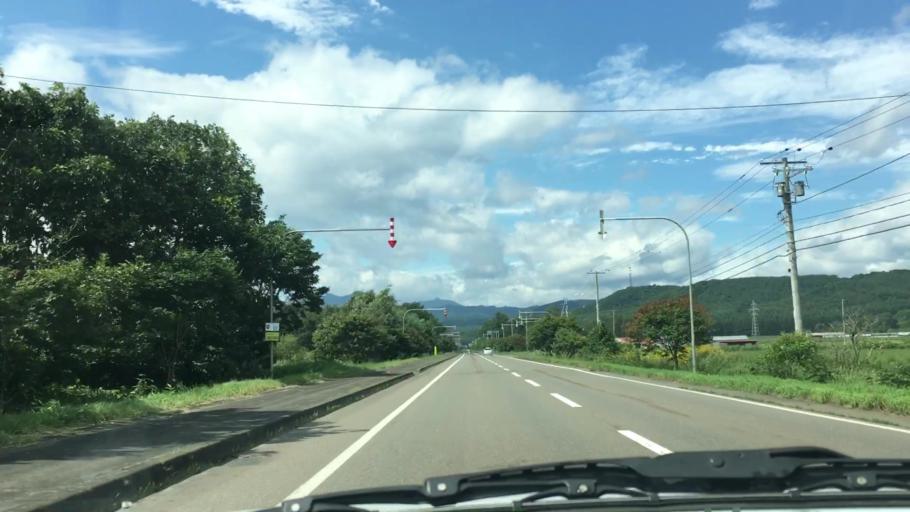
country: JP
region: Hokkaido
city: Otofuke
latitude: 43.3130
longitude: 143.3068
